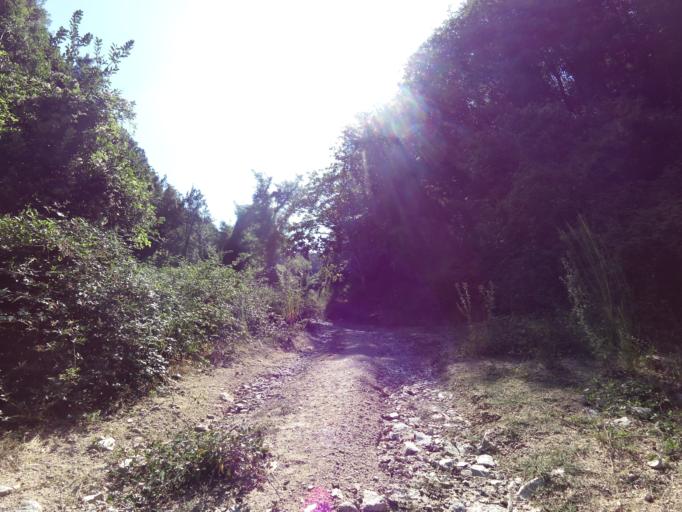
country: IT
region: Calabria
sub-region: Provincia di Reggio Calabria
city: Pazzano
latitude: 38.4698
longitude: 16.4124
